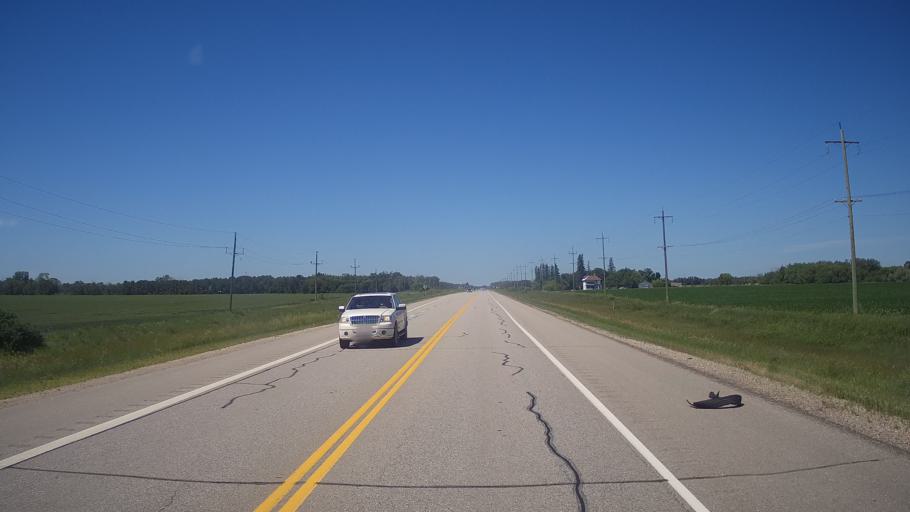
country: CA
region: Manitoba
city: Neepawa
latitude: 50.2253
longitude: -99.3310
